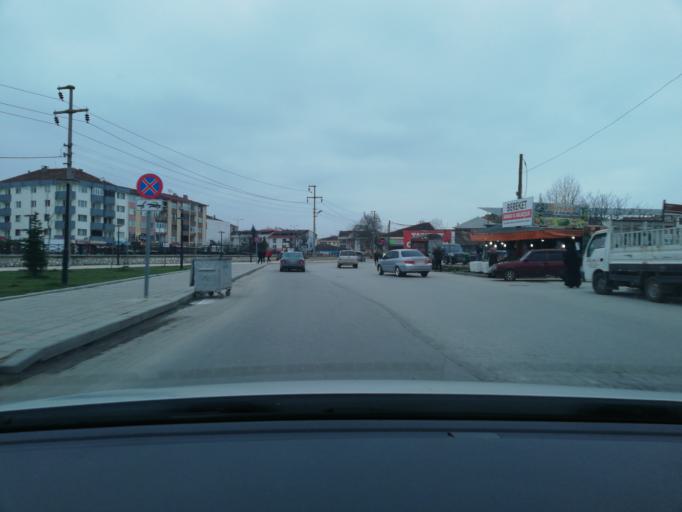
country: TR
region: Duzce
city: Duzce
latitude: 40.8364
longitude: 31.1604
